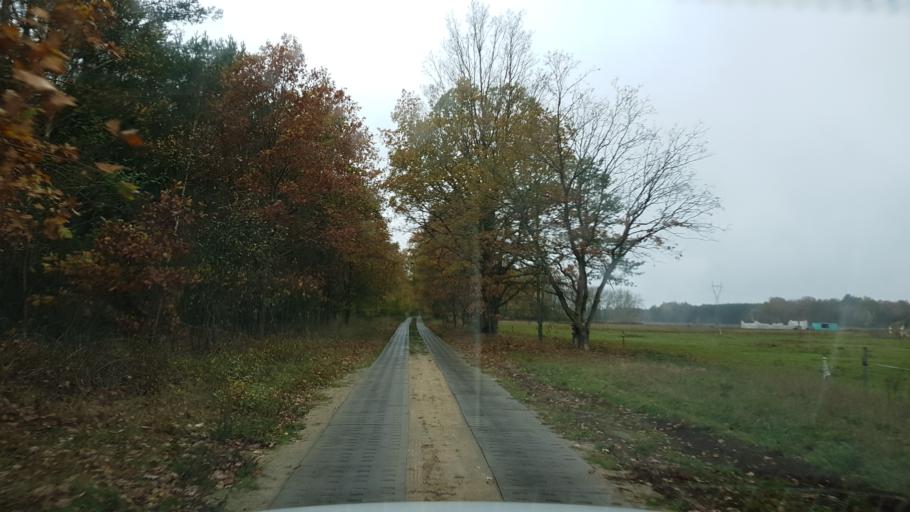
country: PL
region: West Pomeranian Voivodeship
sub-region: Powiat goleniowski
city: Goleniow
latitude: 53.5816
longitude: 14.7739
